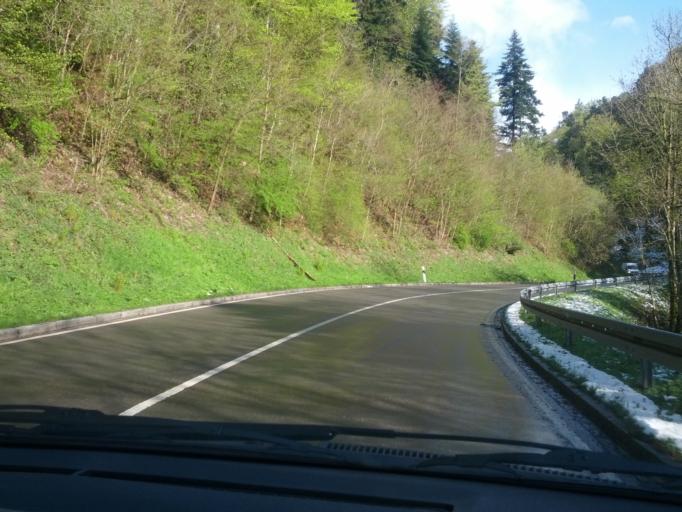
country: DE
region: Baden-Wuerttemberg
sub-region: Freiburg Region
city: Sankt Peter
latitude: 48.0302
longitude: 8.0051
